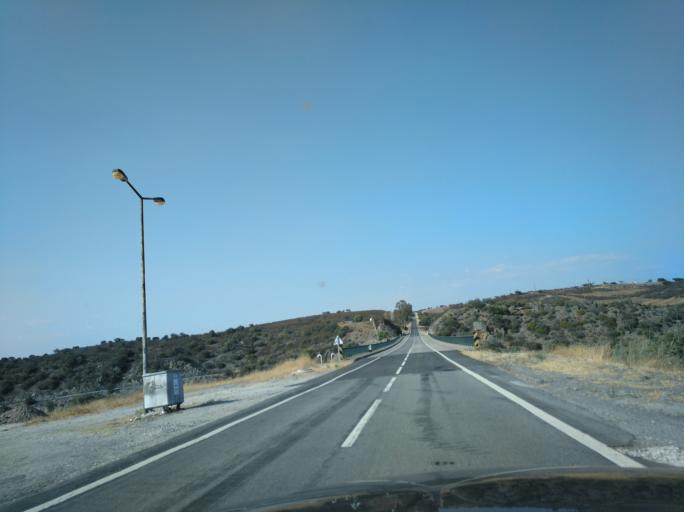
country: ES
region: Extremadura
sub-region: Provincia de Badajoz
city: Valencia del Mombuey
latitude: 38.1501
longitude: -7.2368
